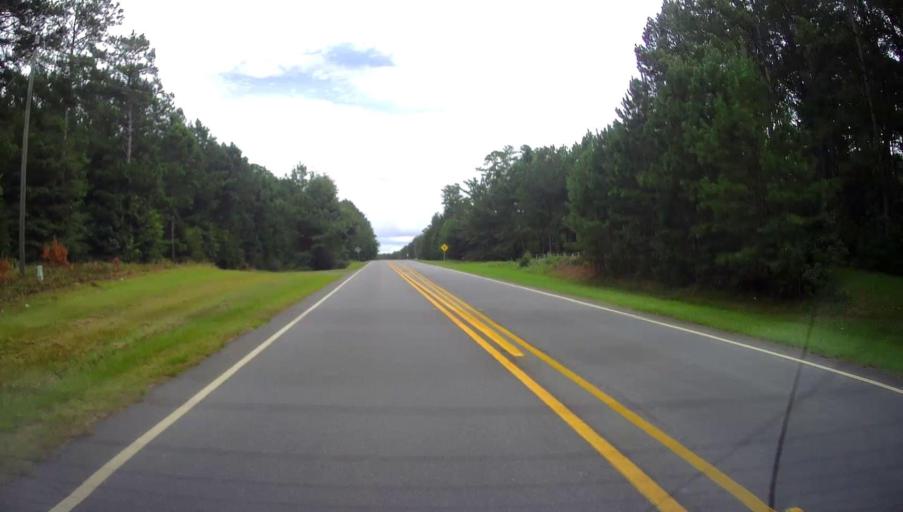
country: US
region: Georgia
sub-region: Schley County
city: Ellaville
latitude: 32.2602
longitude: -84.2492
